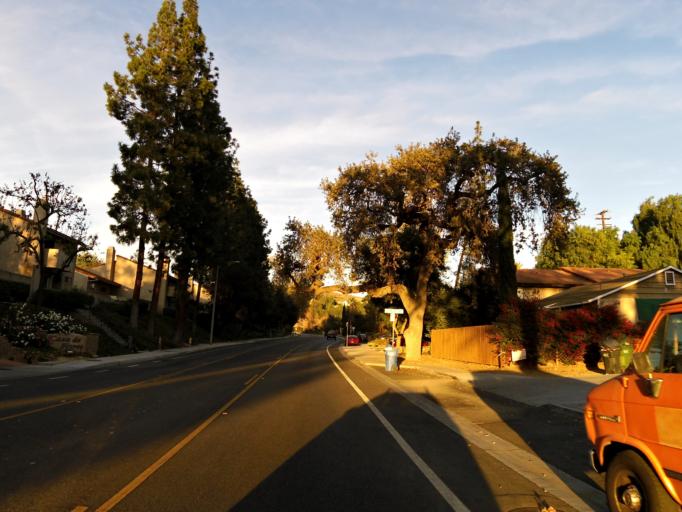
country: US
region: California
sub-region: Ventura County
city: Thousand Oaks
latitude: 34.1788
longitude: -118.8503
